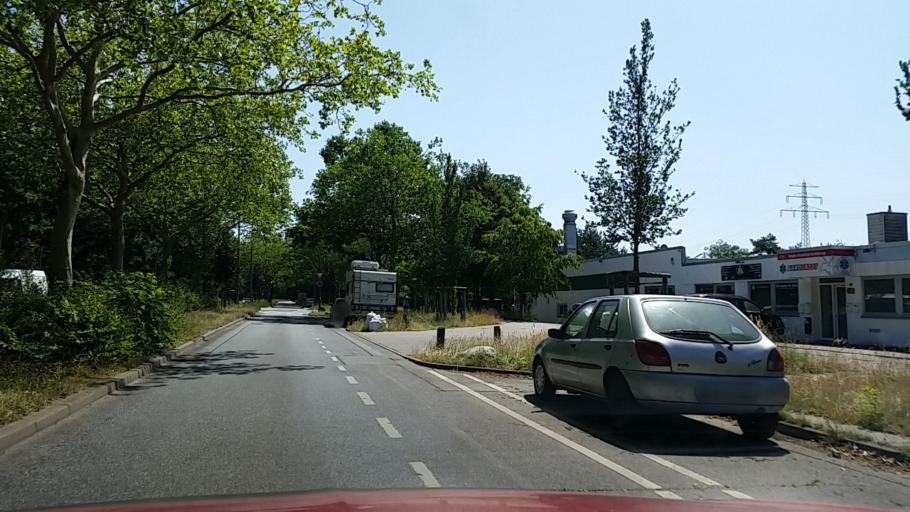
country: DE
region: Hamburg
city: Steilshoop
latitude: 53.6103
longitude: 10.0510
